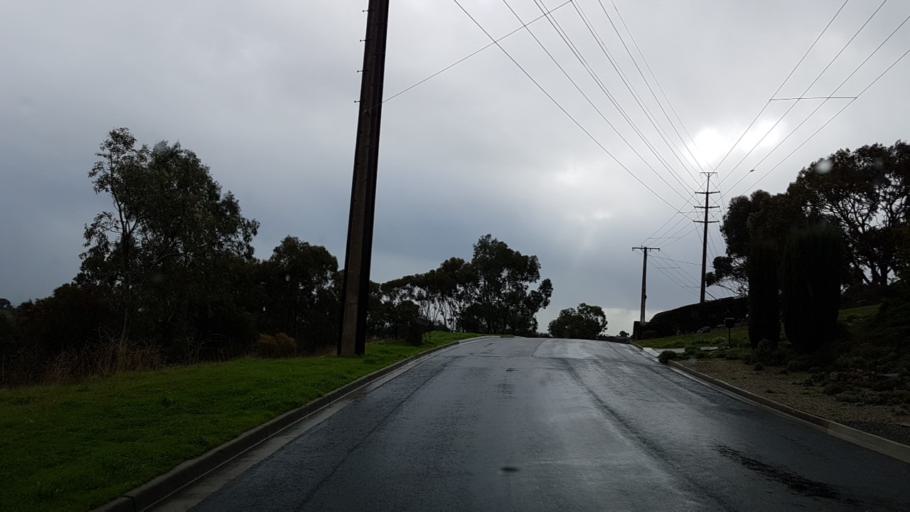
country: AU
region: South Australia
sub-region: Onkaparinga
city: Bedford Park
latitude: -35.0414
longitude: 138.5785
